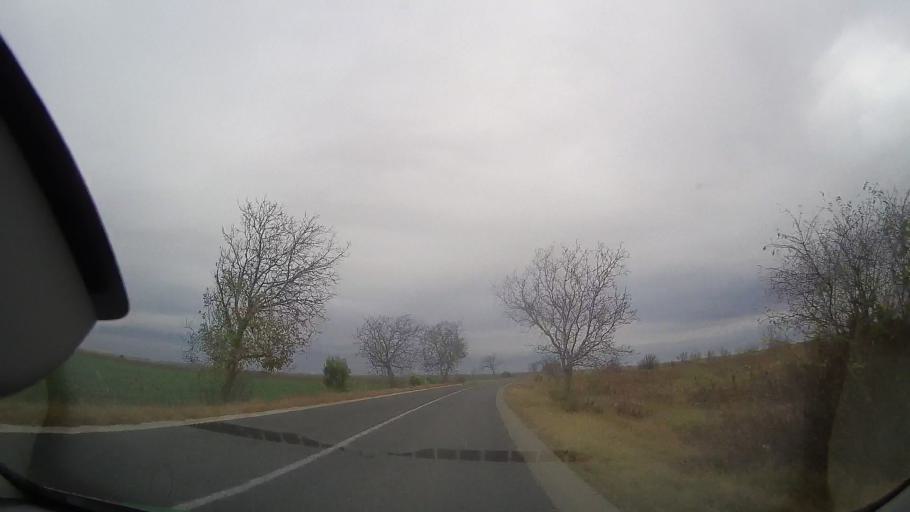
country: RO
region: Ialomita
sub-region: Comuna Milosesti
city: Milosesti
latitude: 44.7746
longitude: 27.1755
